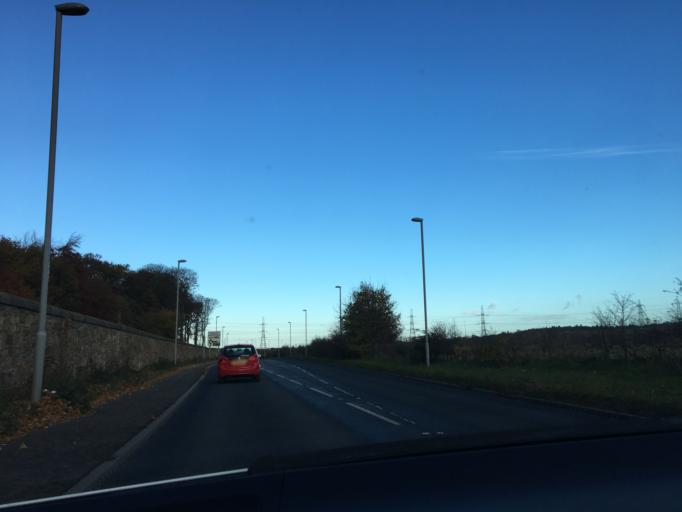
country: GB
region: Scotland
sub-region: Midlothian
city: Dalkeith
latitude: 55.9059
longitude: -3.0480
